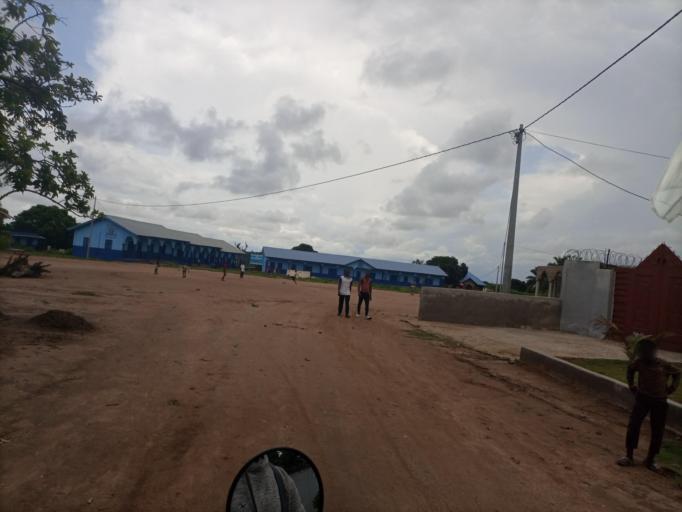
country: SL
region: Northern Province
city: Masoyila
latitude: 8.6048
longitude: -13.1739
